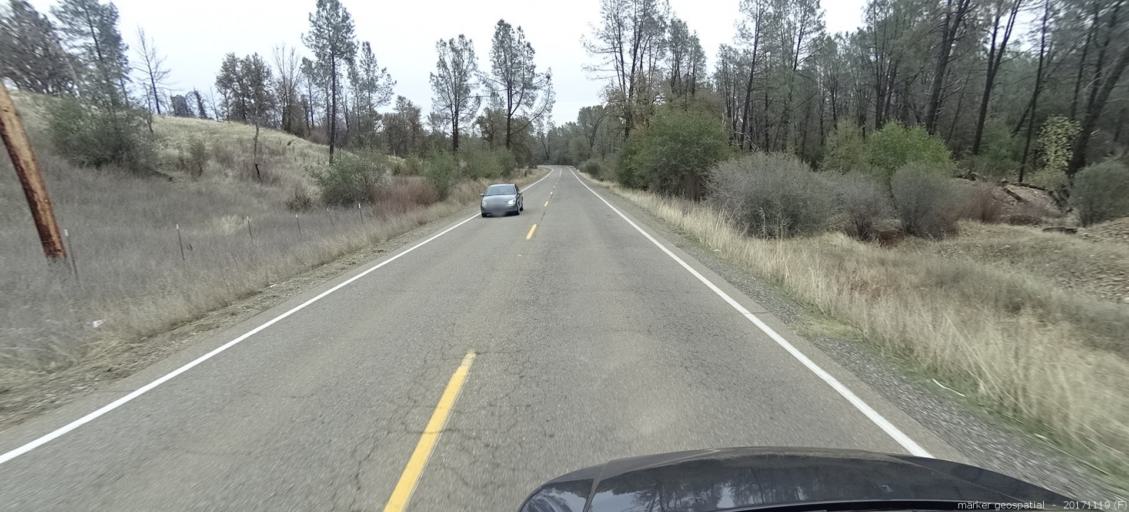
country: US
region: California
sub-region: Shasta County
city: Redding
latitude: 40.4930
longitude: -122.3887
